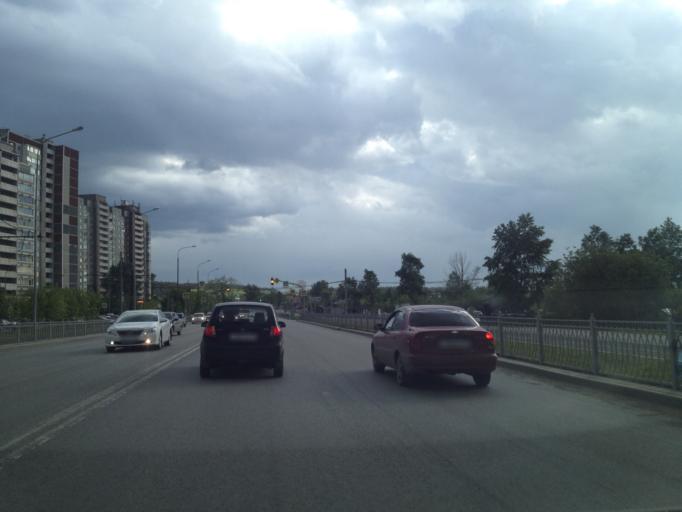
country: RU
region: Sverdlovsk
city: Sovkhoznyy
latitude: 56.8230
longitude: 60.5407
